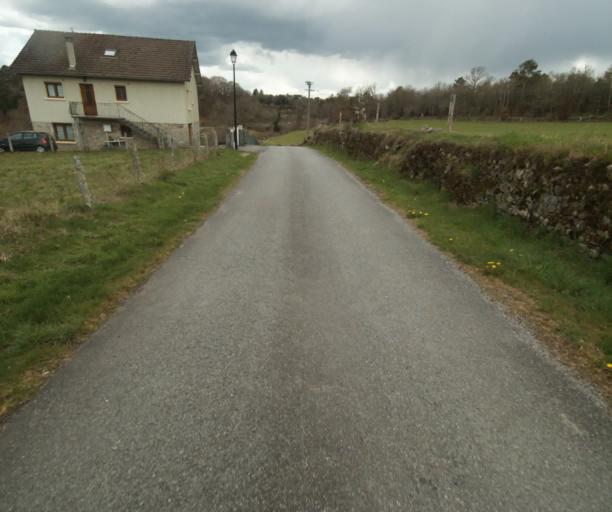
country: FR
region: Limousin
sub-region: Departement de la Correze
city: Correze
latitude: 45.3159
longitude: 1.8871
